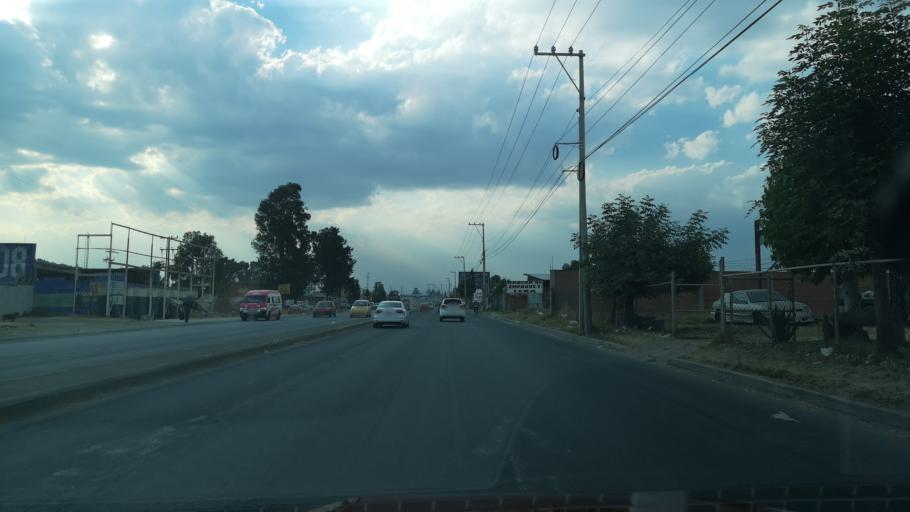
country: MX
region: Puebla
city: Cholula
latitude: 19.0741
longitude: -98.3187
